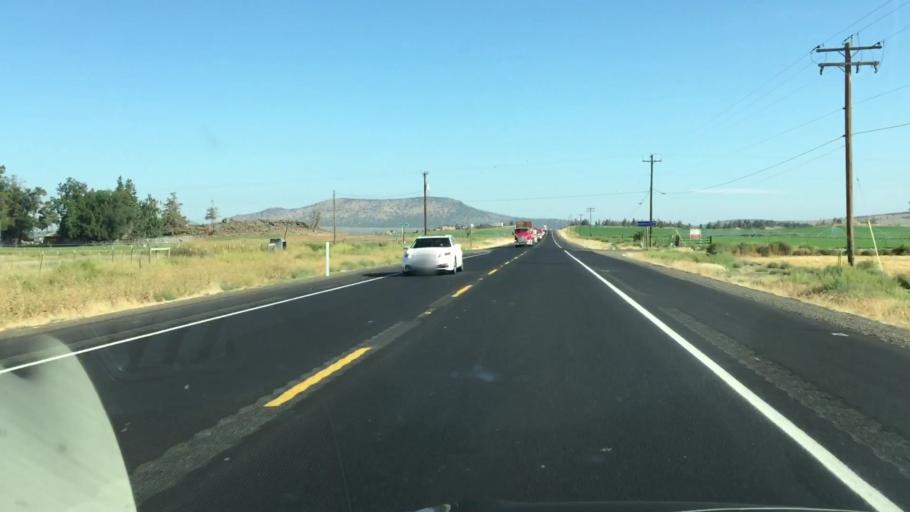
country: US
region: Oregon
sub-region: Deschutes County
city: Terrebonne
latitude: 44.4185
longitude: -121.1991
